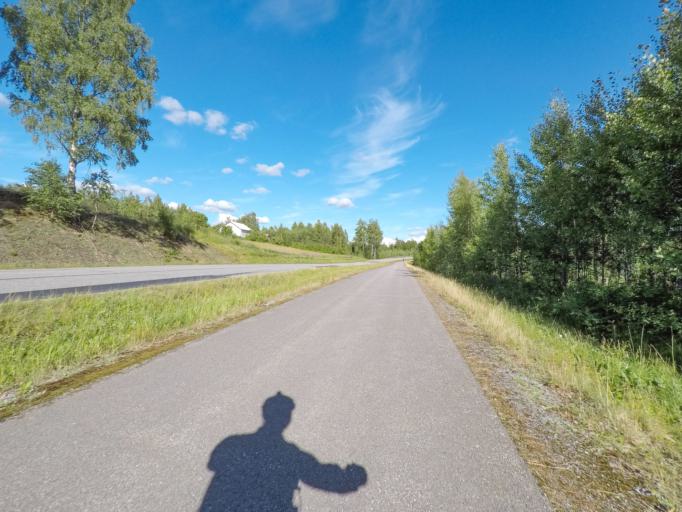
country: FI
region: South Karelia
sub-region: Lappeenranta
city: Joutseno
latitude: 61.1543
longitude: 28.6010
